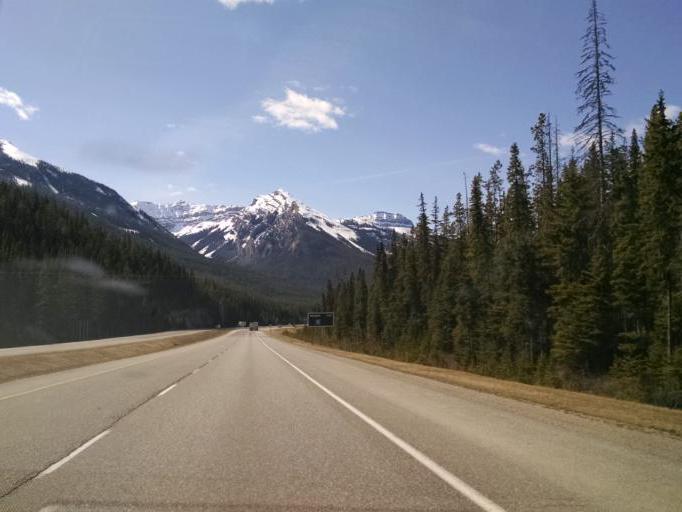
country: CA
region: Alberta
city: Banff
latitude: 51.1581
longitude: -115.6967
